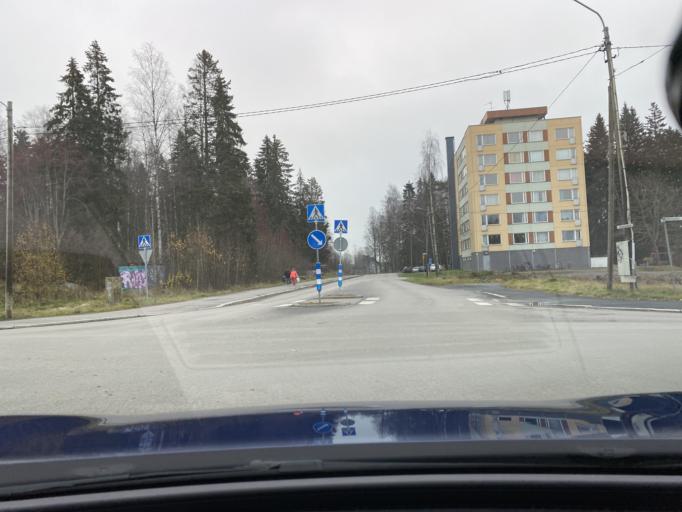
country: FI
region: Pirkanmaa
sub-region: Tampere
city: Nokia
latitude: 61.4598
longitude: 23.5034
